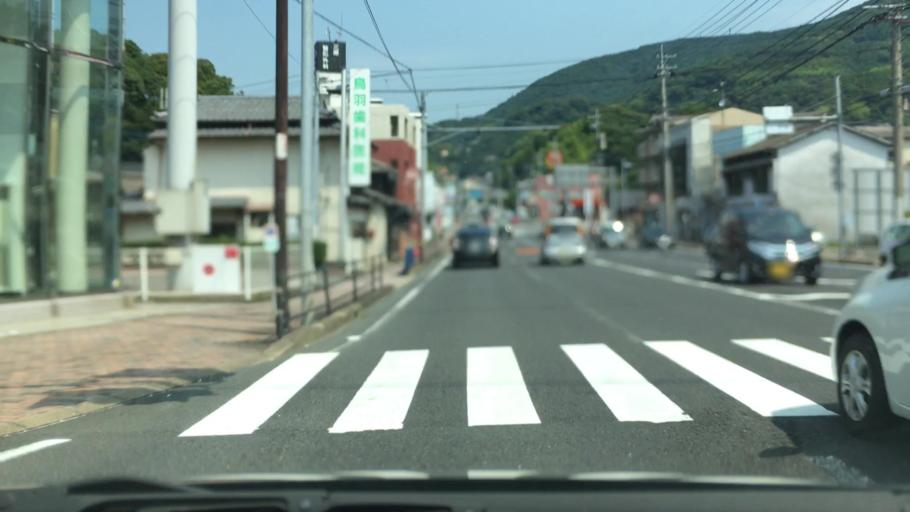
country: JP
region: Nagasaki
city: Sasebo
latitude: 33.1576
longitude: 129.7520
